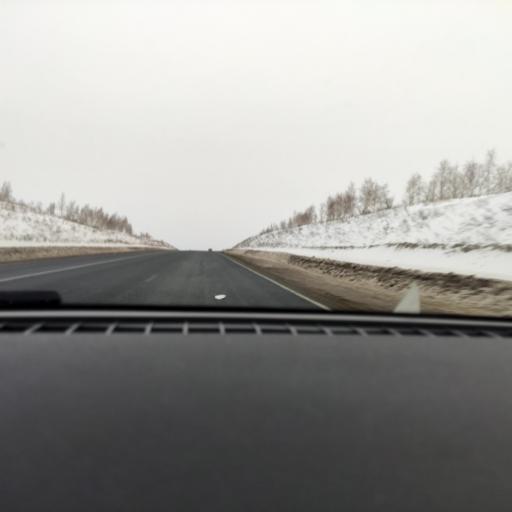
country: RU
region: Samara
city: Novosemeykino
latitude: 53.3676
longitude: 50.4358
